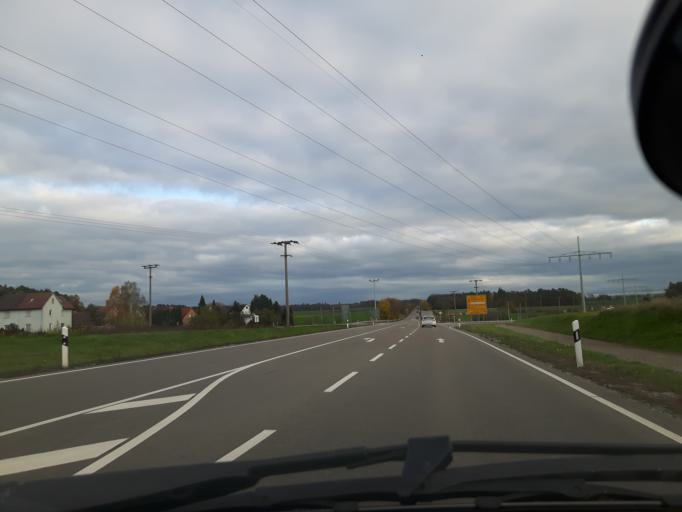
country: DE
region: Bavaria
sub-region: Regierungsbezirk Mittelfranken
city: Burgoberbach
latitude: 49.2314
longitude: 10.6205
